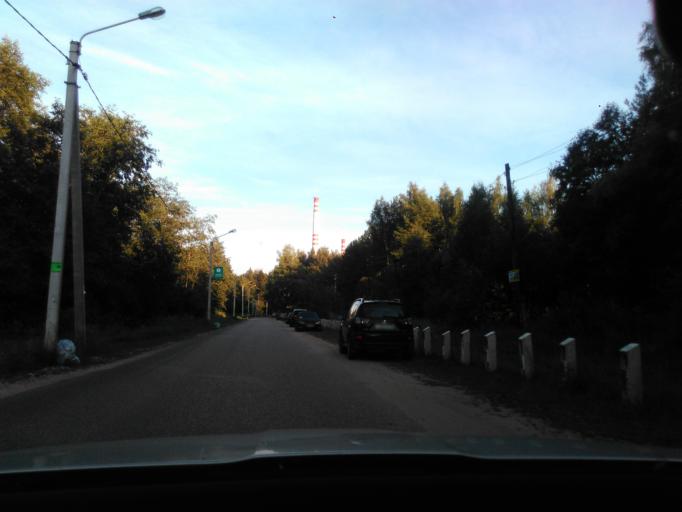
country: RU
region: Tverskaya
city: Konakovo
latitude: 56.7508
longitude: 36.7586
